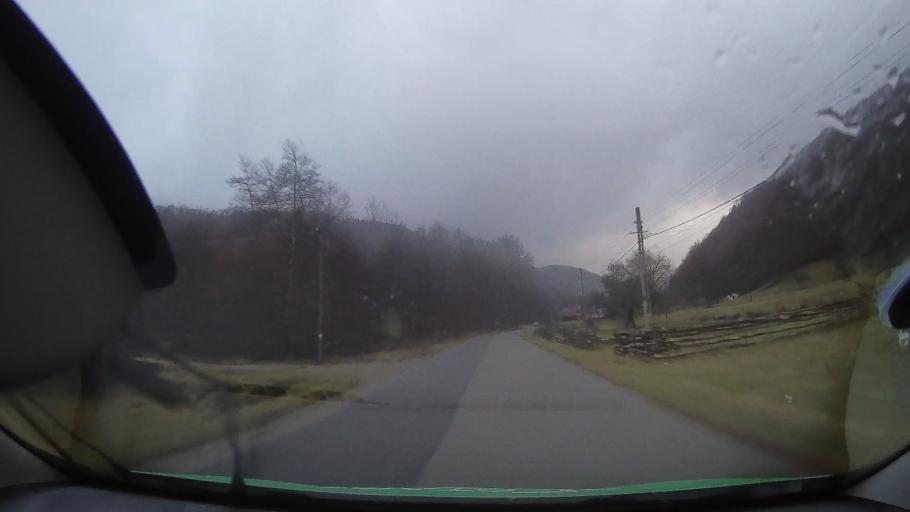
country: RO
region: Hunedoara
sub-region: Comuna Ribita
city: Ribita
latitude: 46.2594
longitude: 22.7449
